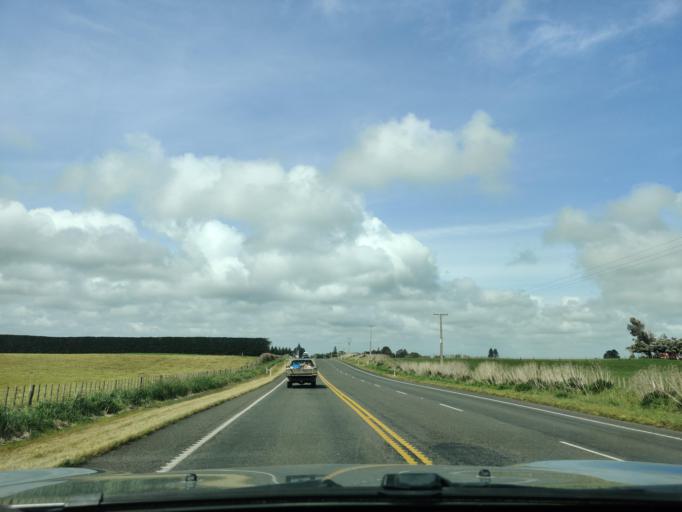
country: NZ
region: Taranaki
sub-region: South Taranaki District
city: Patea
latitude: -39.7656
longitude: 174.6158
